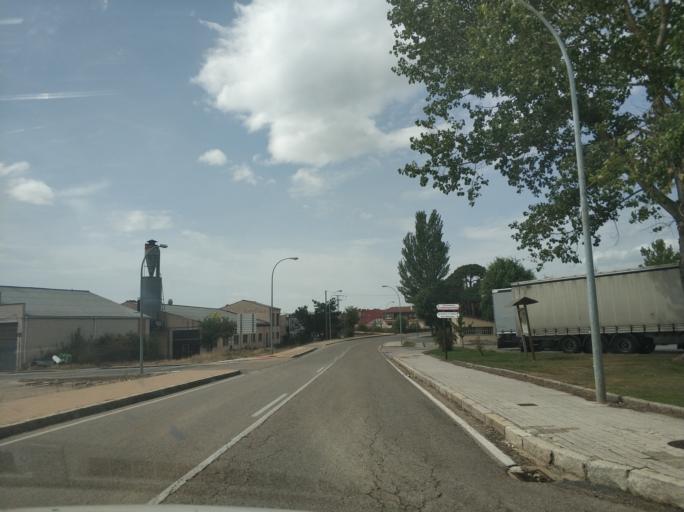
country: ES
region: Castille and Leon
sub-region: Provincia de Soria
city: Duruelo de la Sierra
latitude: 41.9524
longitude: -2.9273
